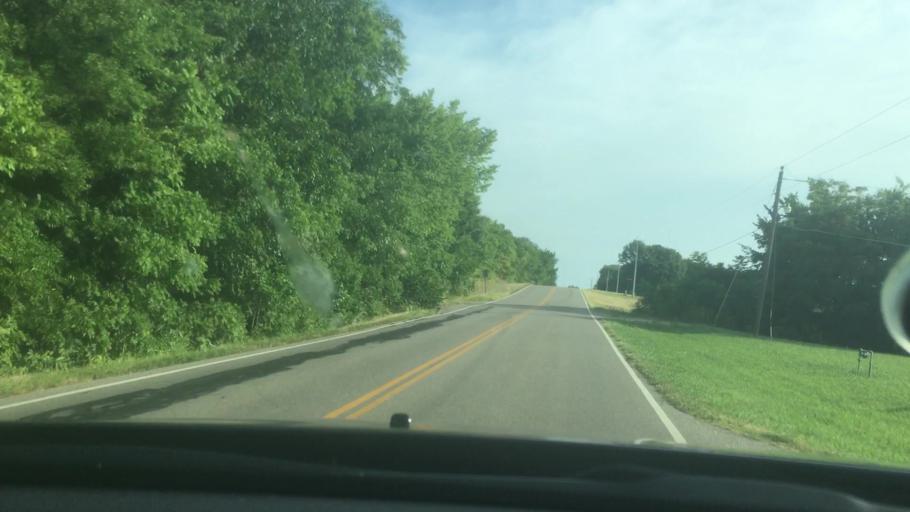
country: US
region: Oklahoma
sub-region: Pontotoc County
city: Ada
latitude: 34.7286
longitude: -96.6700
